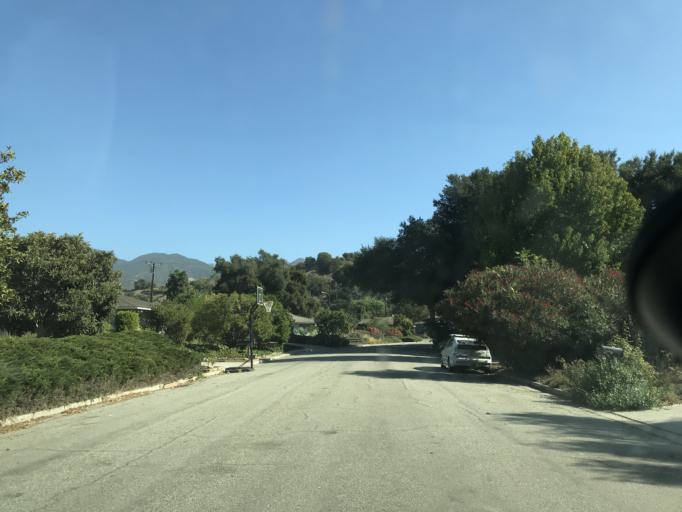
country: US
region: California
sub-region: Santa Barbara County
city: Goleta
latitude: 34.4540
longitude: -119.7973
